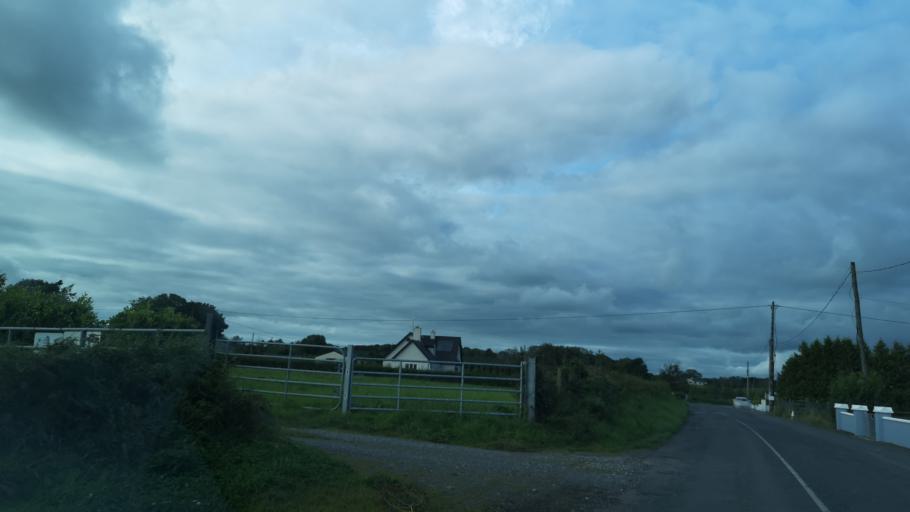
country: IE
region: Connaught
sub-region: County Galway
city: Ballinasloe
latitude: 53.2988
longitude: -8.1021
